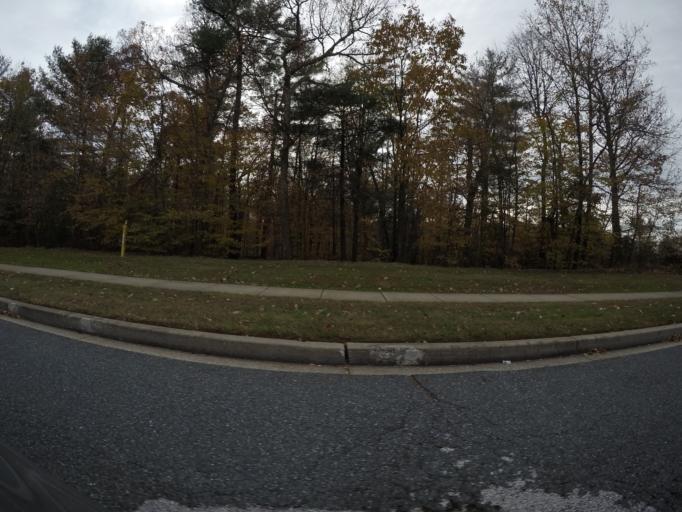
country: US
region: Maryland
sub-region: Harford County
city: Bel Air South
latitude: 39.4703
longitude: -76.2983
